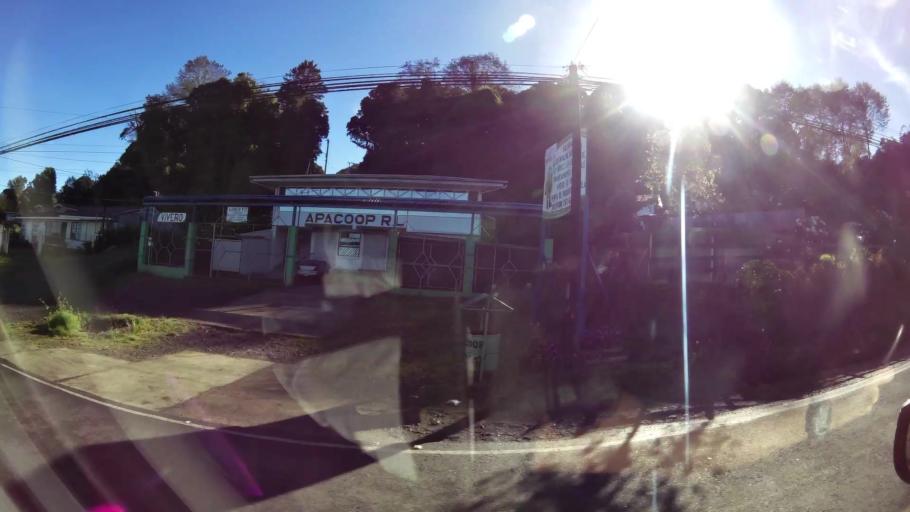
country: CR
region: San Jose
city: San Marcos
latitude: 9.7185
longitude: -83.9496
